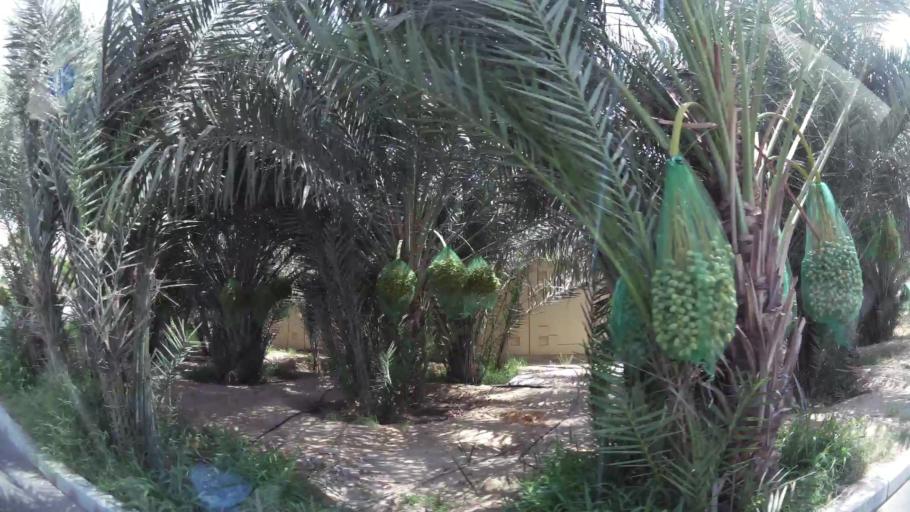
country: AE
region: Ash Shariqah
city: Sharjah
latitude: 25.2478
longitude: 55.4253
